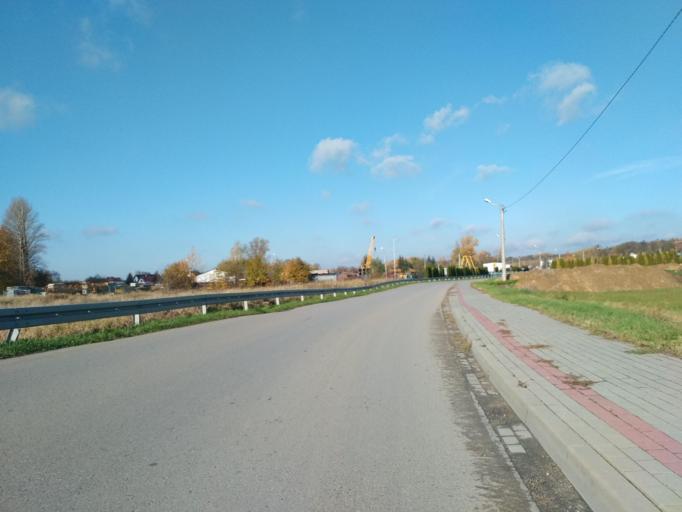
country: PL
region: Subcarpathian Voivodeship
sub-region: Powiat rzeszowski
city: Niechobrz
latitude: 50.0170
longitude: 21.8853
